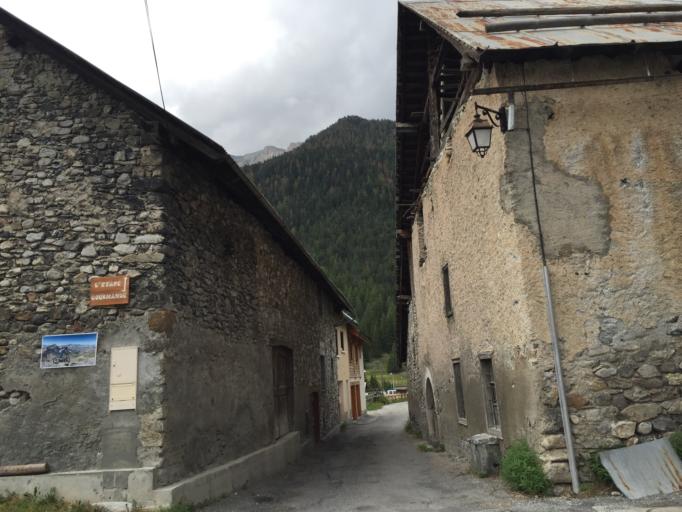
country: FR
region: Provence-Alpes-Cote d'Azur
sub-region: Departement des Hautes-Alpes
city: Guillestre
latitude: 44.6669
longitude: 6.7770
